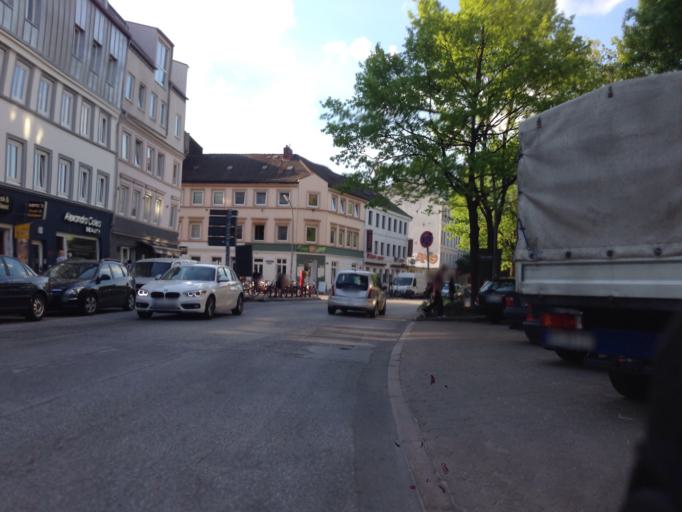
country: DE
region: Hamburg
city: Altona
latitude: 53.5566
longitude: 9.9283
